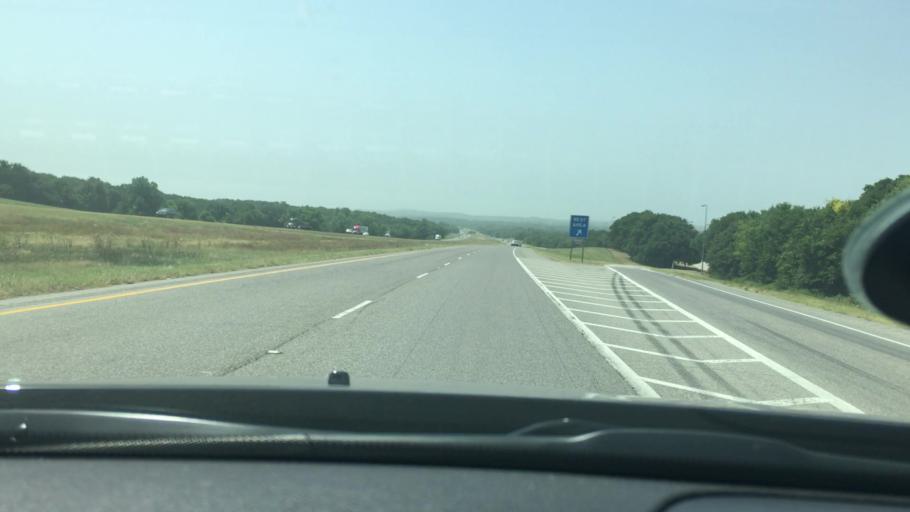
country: US
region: Oklahoma
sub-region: Murray County
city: Davis
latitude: 34.5519
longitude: -97.1915
